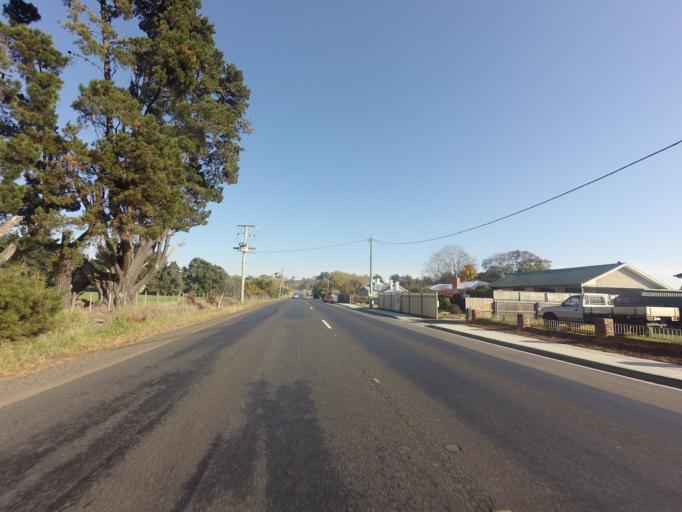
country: AU
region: Tasmania
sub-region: Northern Midlands
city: Perth
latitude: -41.5770
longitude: 147.1648
